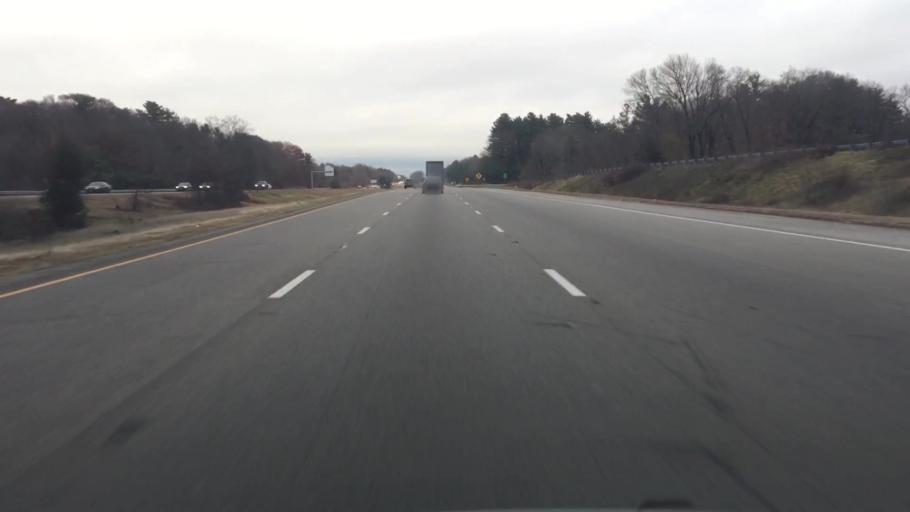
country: US
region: Massachusetts
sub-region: Bristol County
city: Mansfield Center
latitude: 42.0003
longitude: -71.2106
